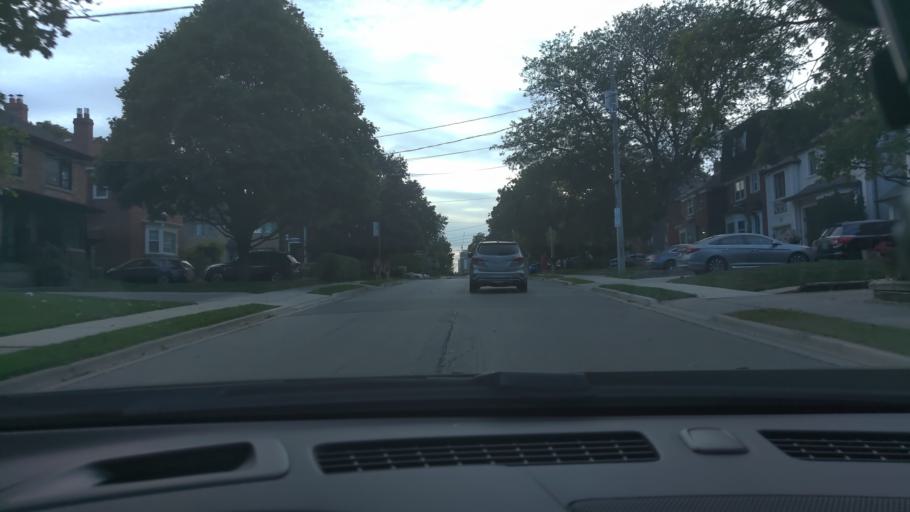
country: CA
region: Ontario
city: Toronto
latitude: 43.7168
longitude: -79.3747
